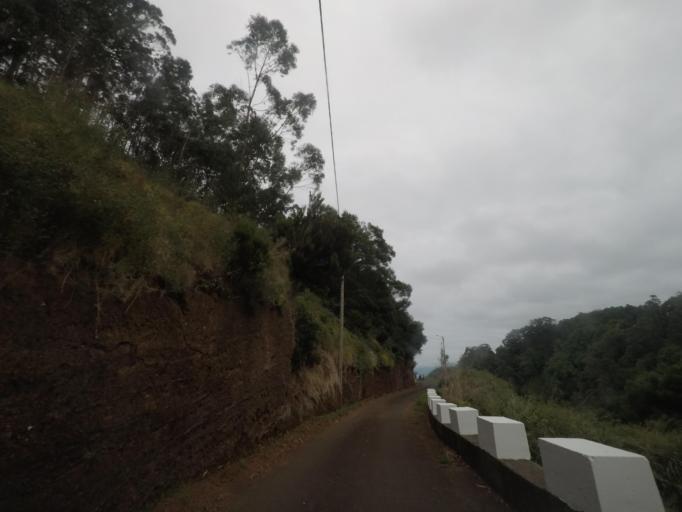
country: PT
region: Madeira
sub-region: Porto Moniz
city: Porto Moniz
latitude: 32.8622
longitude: -17.1820
